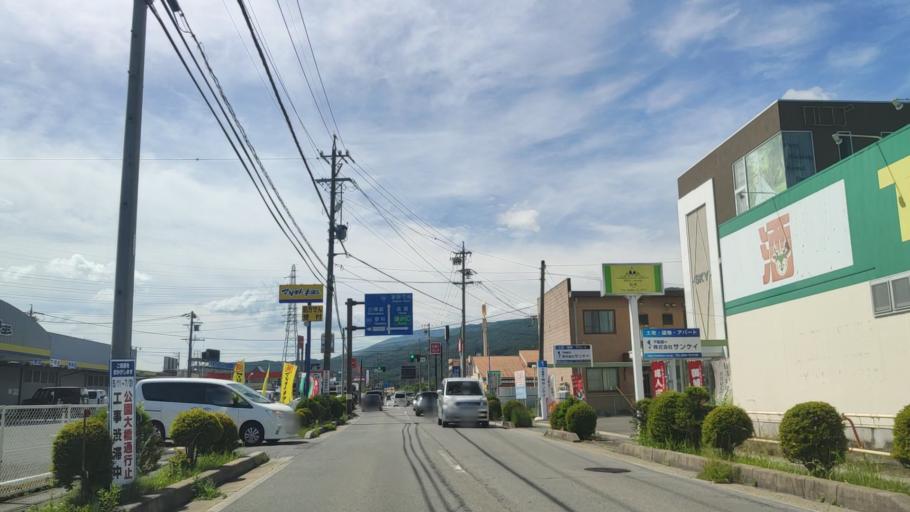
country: JP
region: Nagano
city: Chino
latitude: 35.9989
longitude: 138.1427
